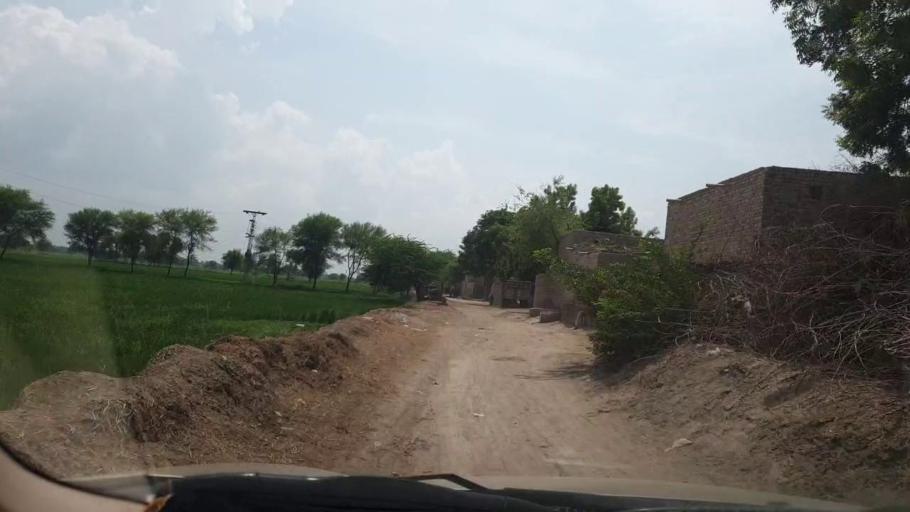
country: PK
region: Sindh
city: Larkana
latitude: 27.5924
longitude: 68.1215
